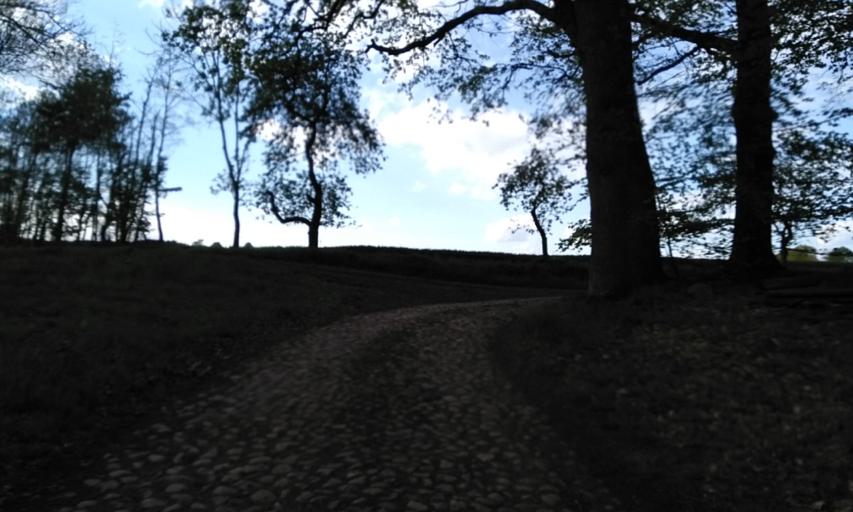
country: DE
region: Lower Saxony
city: Regesbostel
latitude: 53.4087
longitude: 9.6429
